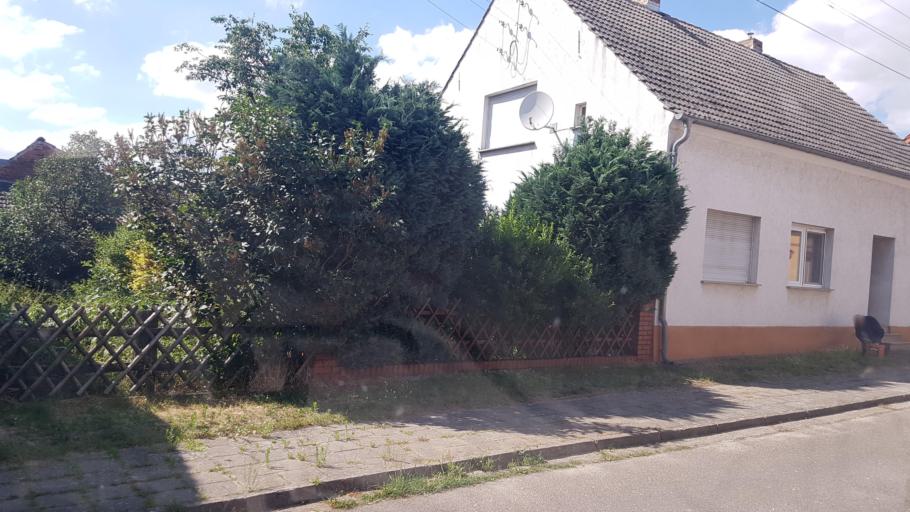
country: DE
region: Saxony-Anhalt
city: Holzdorf
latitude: 51.8571
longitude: 13.1048
